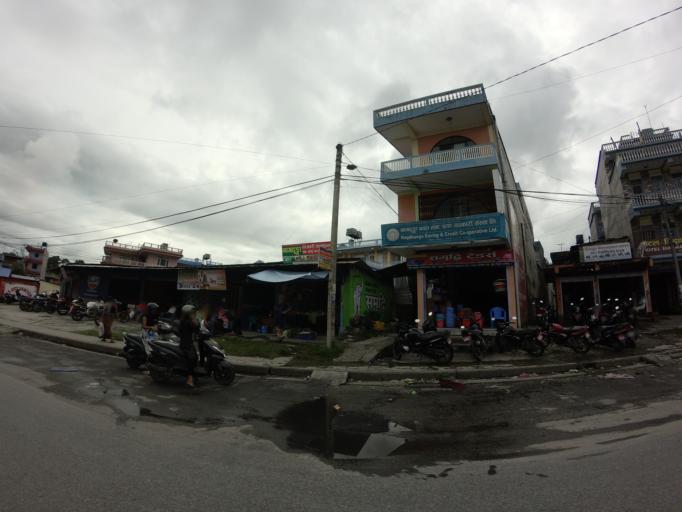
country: NP
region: Western Region
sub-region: Gandaki Zone
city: Pokhara
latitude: 28.2049
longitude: 83.9828
